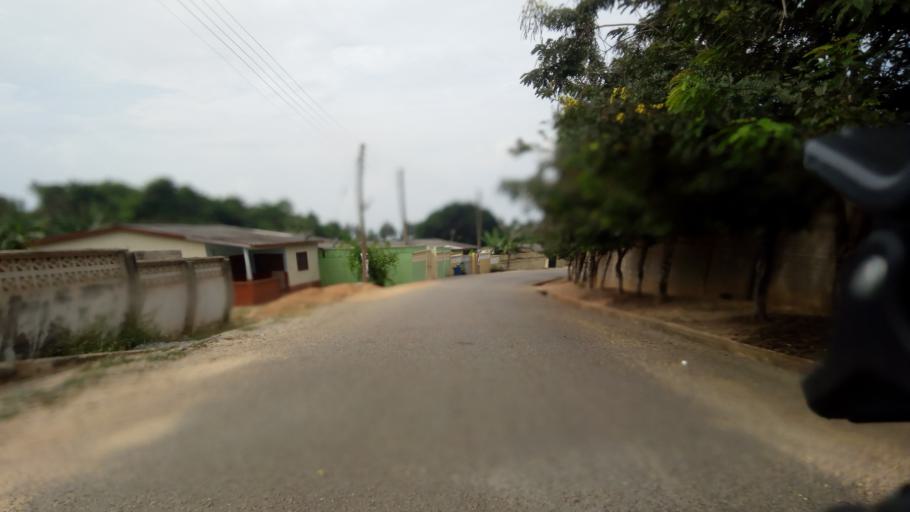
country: GH
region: Central
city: Cape Coast
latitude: 5.1046
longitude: -1.2759
